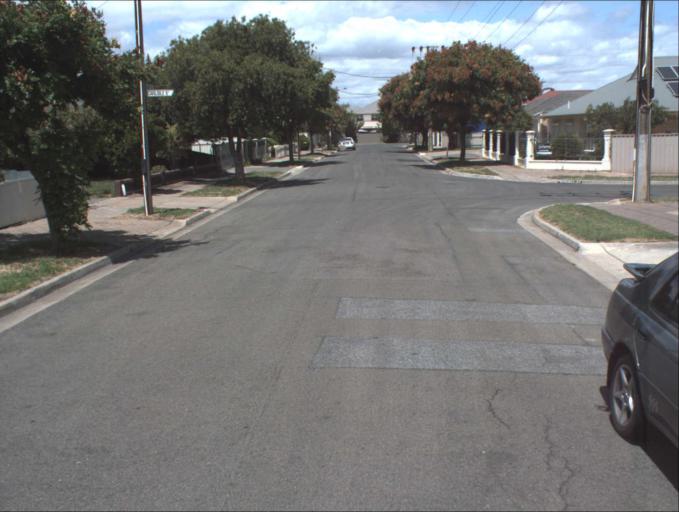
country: AU
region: South Australia
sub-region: Port Adelaide Enfield
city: Enfield
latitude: -34.8571
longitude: 138.6259
